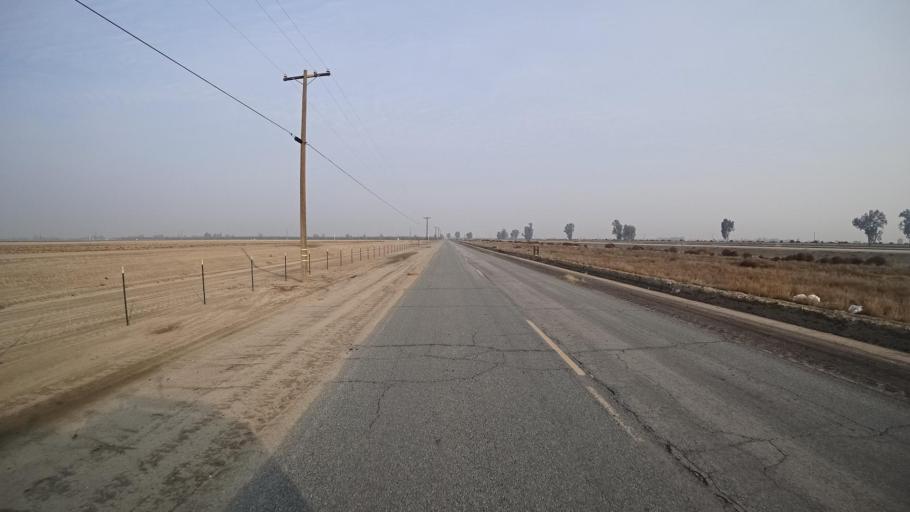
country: US
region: California
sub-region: Kern County
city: Greenfield
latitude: 35.2457
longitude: -119.0214
